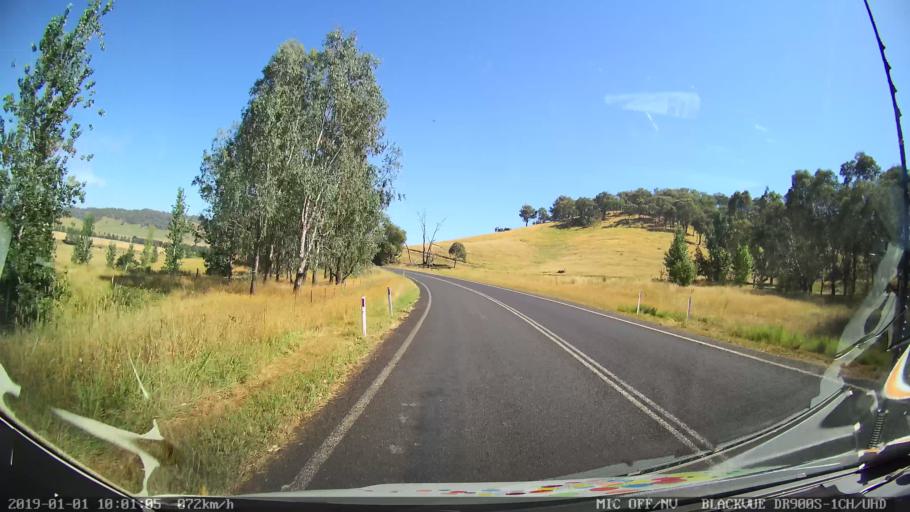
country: AU
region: New South Wales
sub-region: Snowy River
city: Jindabyne
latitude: -36.1950
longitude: 148.1030
